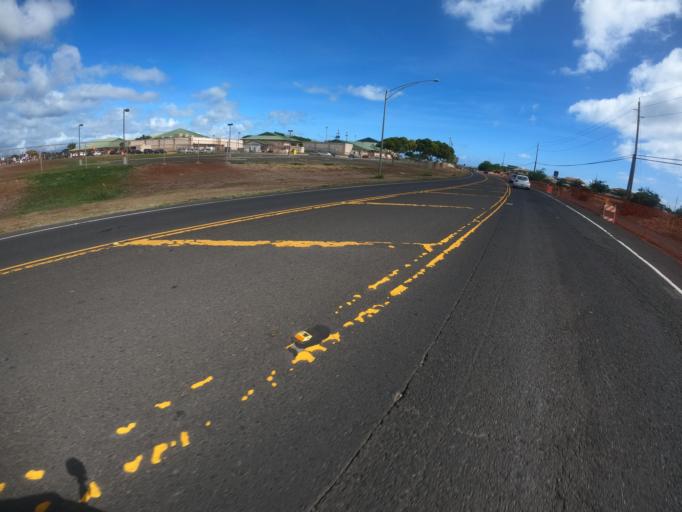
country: US
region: Hawaii
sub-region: Honolulu County
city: Makakilo City
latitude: 21.3285
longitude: -158.0712
